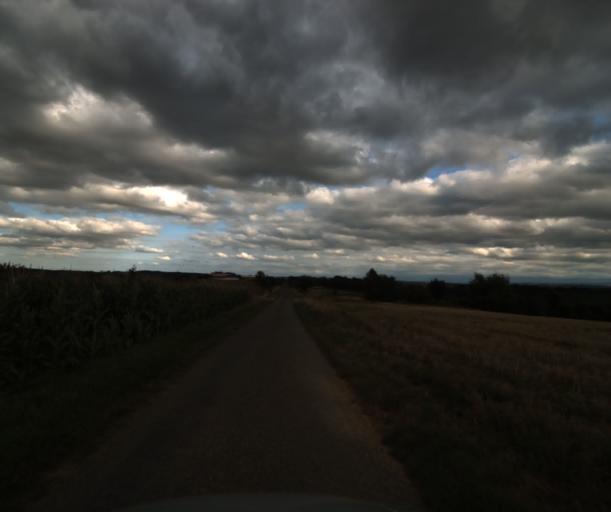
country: FR
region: Midi-Pyrenees
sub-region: Departement de la Haute-Garonne
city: Le Fauga
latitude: 43.3946
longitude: 1.3181
